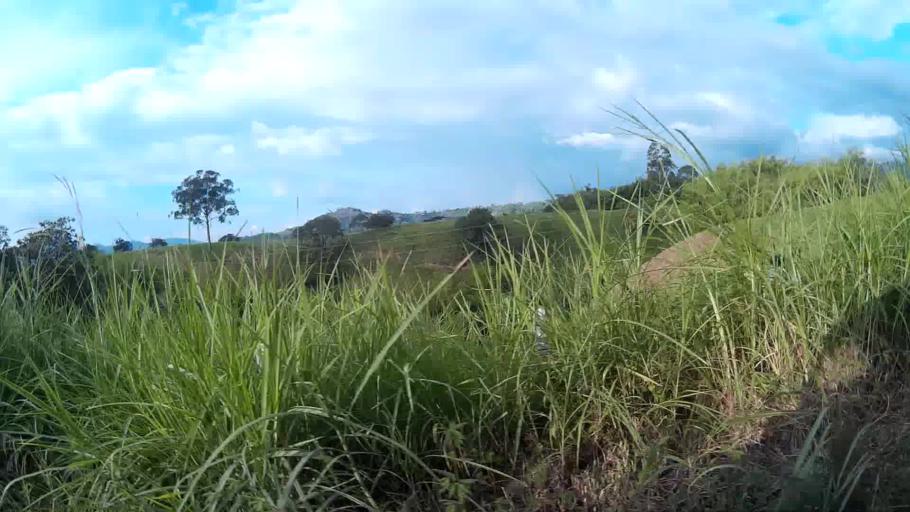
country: CO
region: Valle del Cauca
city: Ulloa
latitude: 4.7498
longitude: -75.7428
